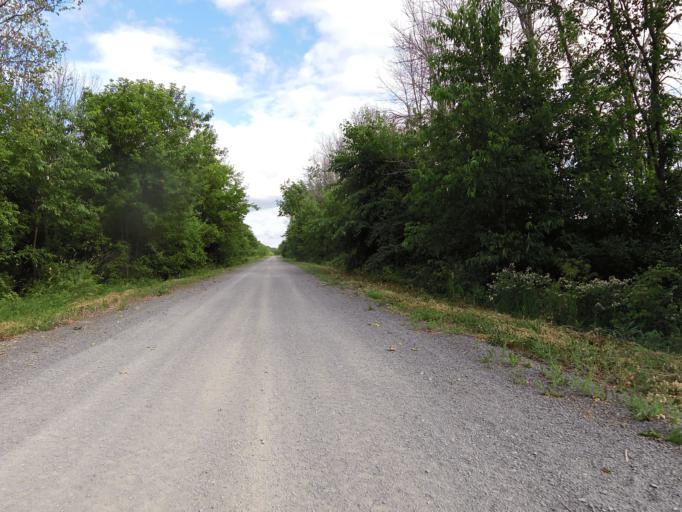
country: CA
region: Ontario
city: Arnprior
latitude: 45.3082
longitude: -76.2761
